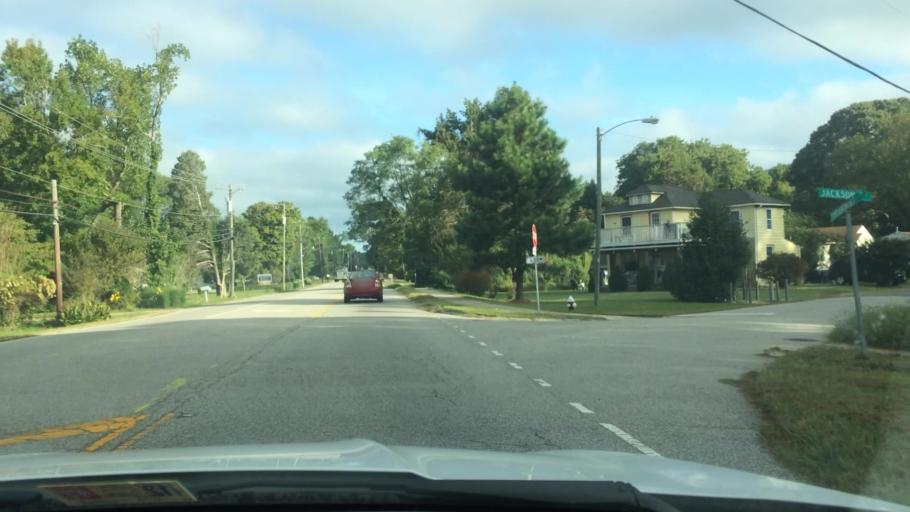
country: US
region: Virginia
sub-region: City of Williamsburg
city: Williamsburg
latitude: 37.2233
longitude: -76.6260
